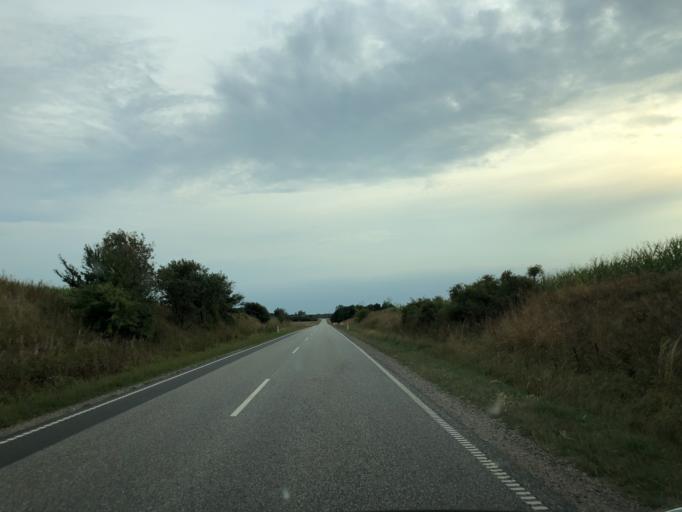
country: DK
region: Central Jutland
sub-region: Struer Kommune
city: Struer
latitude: 56.4129
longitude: 8.4830
